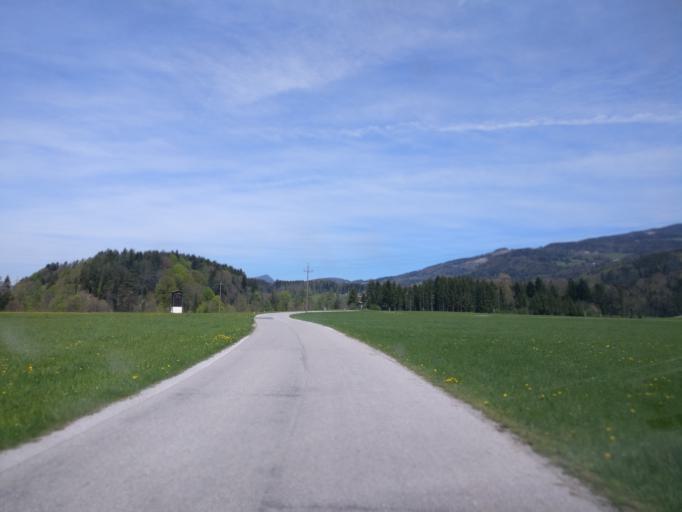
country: AT
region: Salzburg
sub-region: Politischer Bezirk Hallein
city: Kuchl
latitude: 47.6522
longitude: 13.1482
